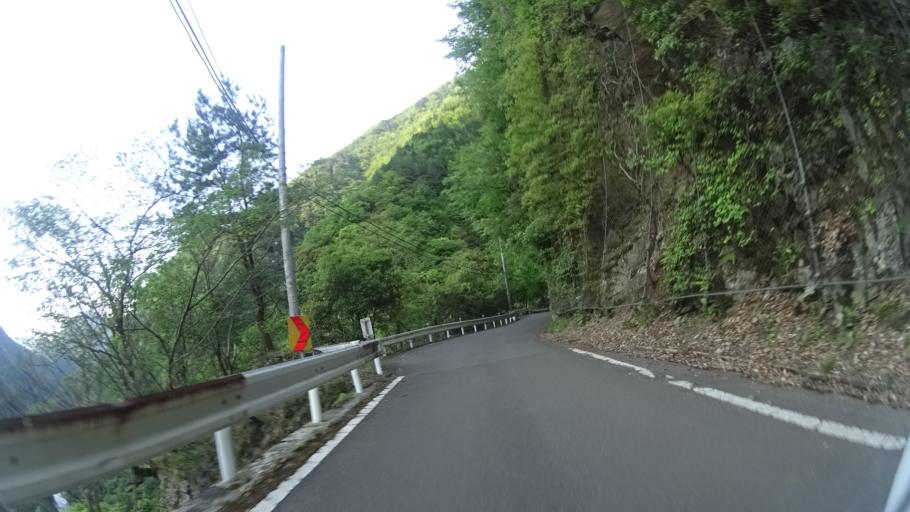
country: JP
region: Tokushima
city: Ikedacho
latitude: 33.9259
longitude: 133.8187
